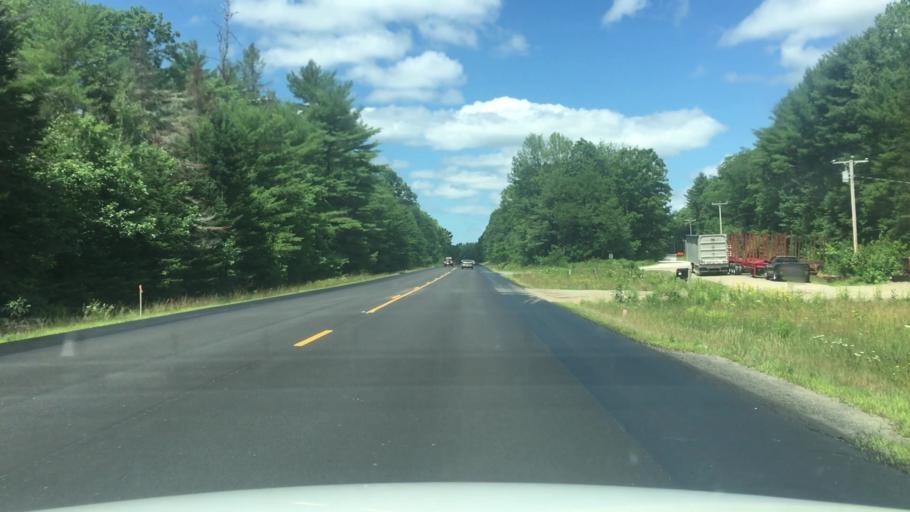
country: US
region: Maine
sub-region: Waldo County
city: Searsmont
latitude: 44.4052
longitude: -69.1688
